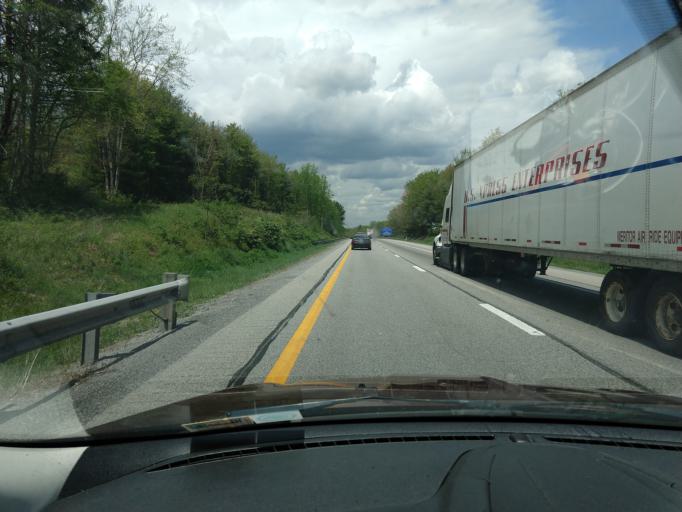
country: US
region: West Virginia
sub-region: Mercer County
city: Athens
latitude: 37.4005
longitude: -81.0609
